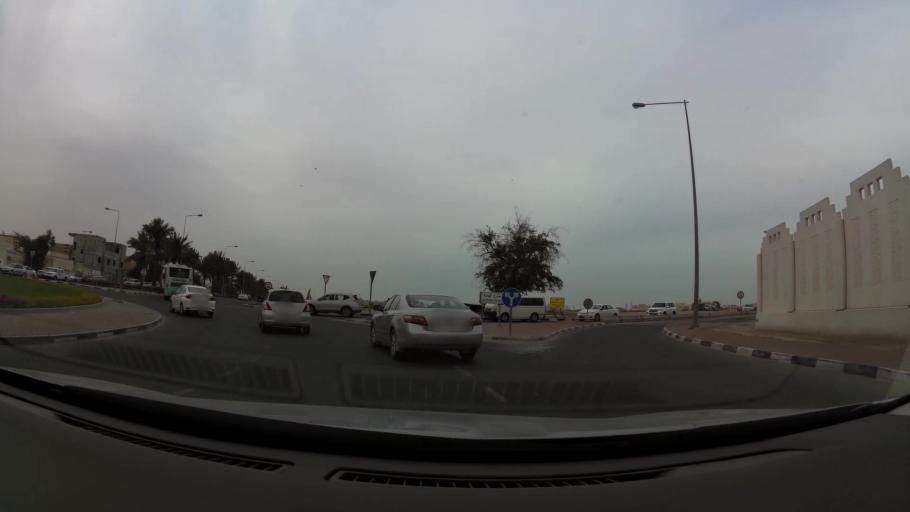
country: QA
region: Baladiyat ad Dawhah
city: Doha
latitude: 25.3148
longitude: 51.4873
